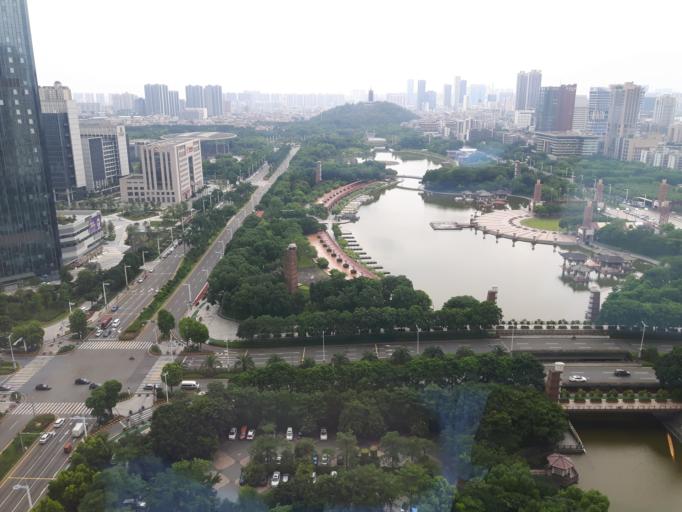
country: CN
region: Guangdong
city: Foshan
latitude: 23.0594
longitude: 113.1427
